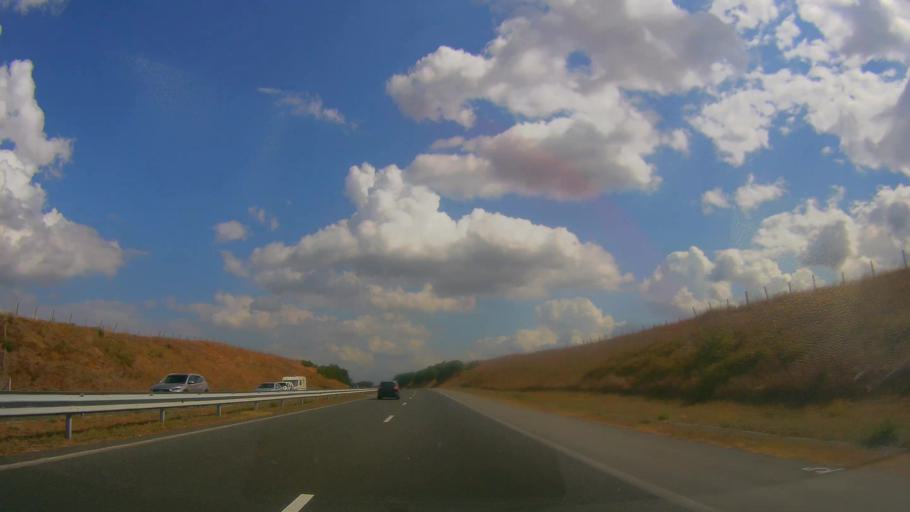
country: BG
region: Yambol
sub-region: Obshtina Yambol
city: Yambol
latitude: 42.5413
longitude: 26.4656
